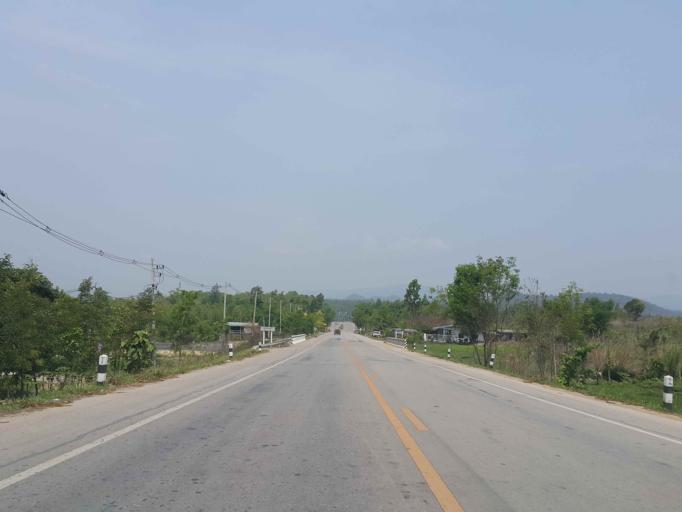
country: TH
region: Chiang Mai
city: Mae Taeng
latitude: 19.0839
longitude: 98.9111
